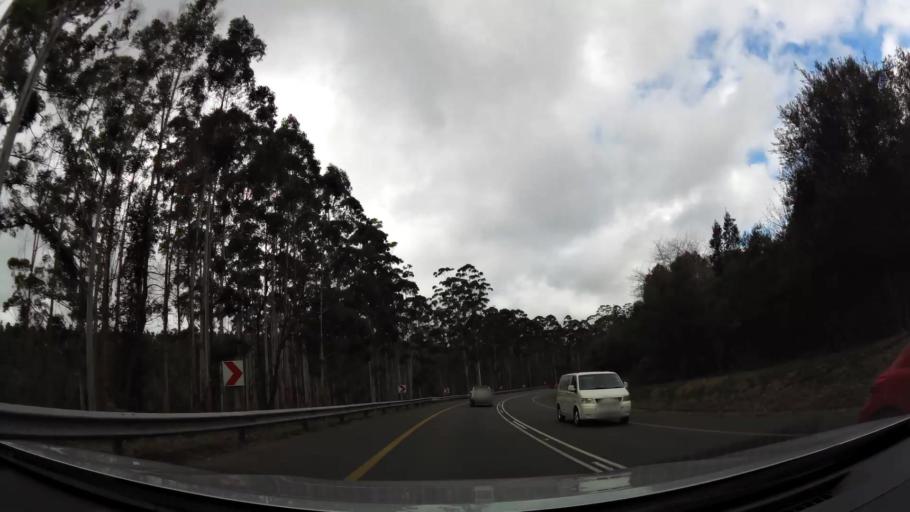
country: ZA
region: Western Cape
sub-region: Eden District Municipality
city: Knysna
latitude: -34.0246
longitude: 23.1625
